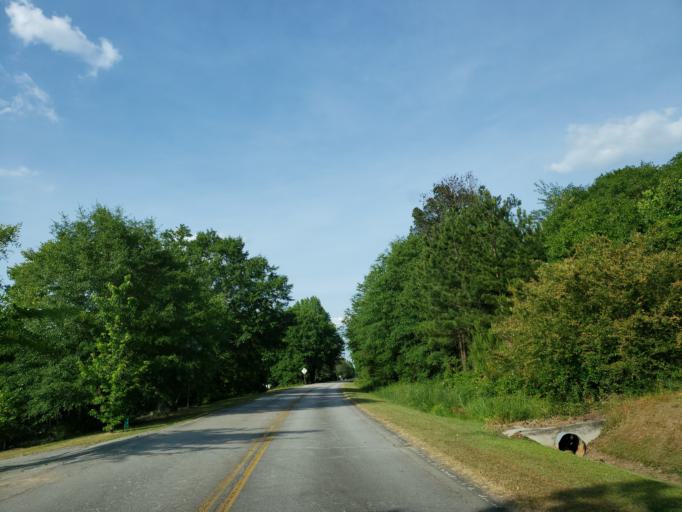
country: US
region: Georgia
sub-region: Carroll County
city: Carrollton
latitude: 33.4606
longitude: -85.1280
